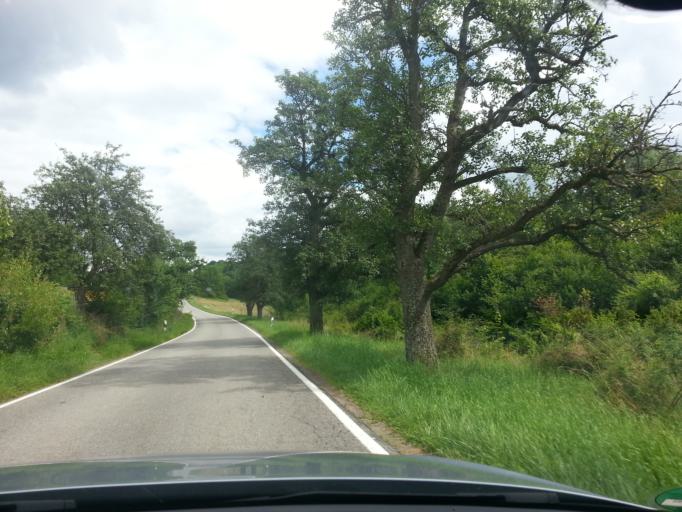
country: DE
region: Saarland
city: Beckingen
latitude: 49.4382
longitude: 6.6864
